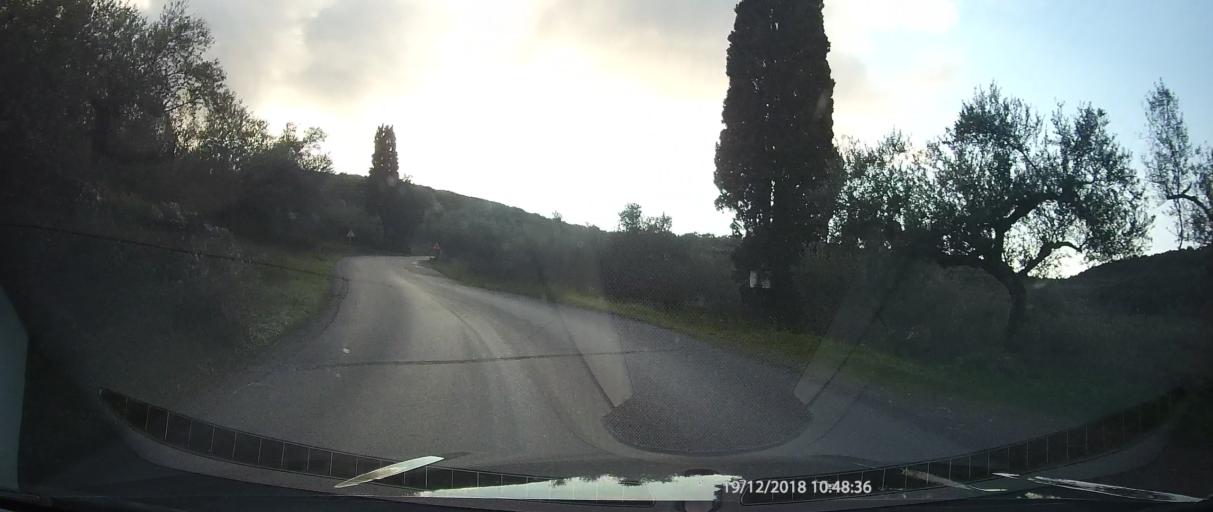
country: GR
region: Peloponnese
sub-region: Nomos Messinias
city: Kardamyli
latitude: 36.9297
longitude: 22.1898
